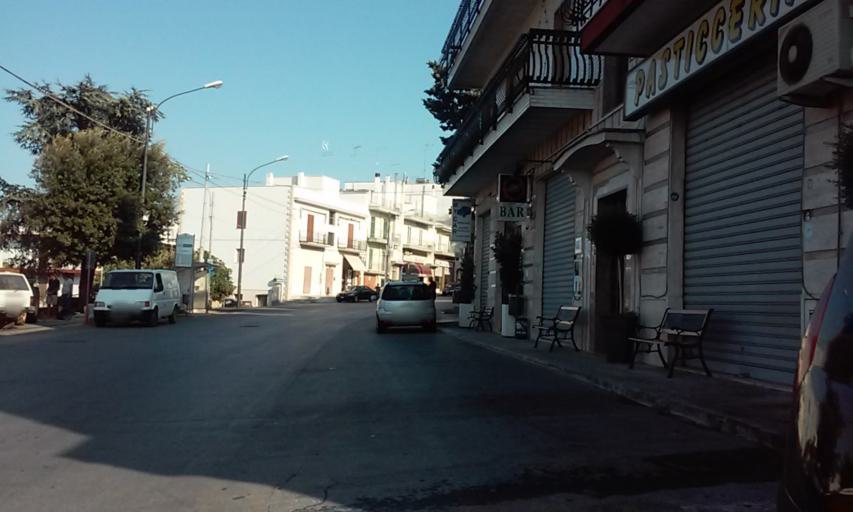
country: IT
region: Apulia
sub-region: Provincia di Brindisi
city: Ceglie Messapica
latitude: 40.6502
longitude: 17.5103
